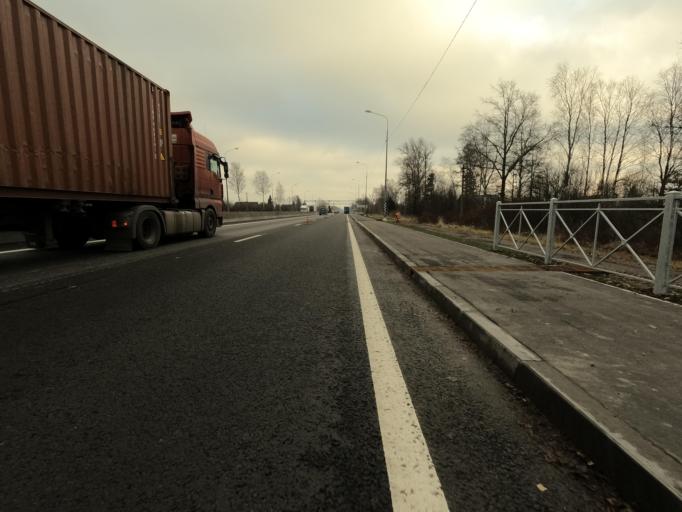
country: RU
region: Leningrad
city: Mga
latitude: 59.7210
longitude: 31.1012
